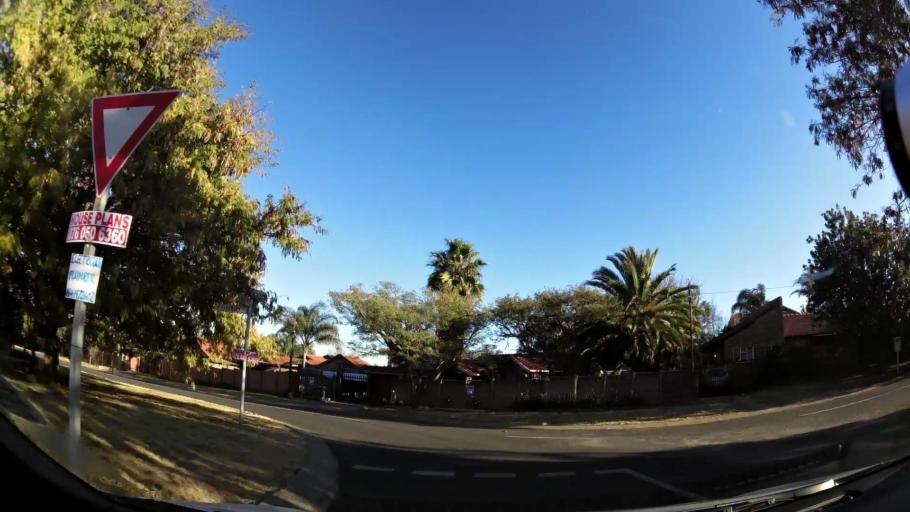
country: ZA
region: Gauteng
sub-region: City of Tshwane Metropolitan Municipality
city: Centurion
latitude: -25.9025
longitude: 28.1362
